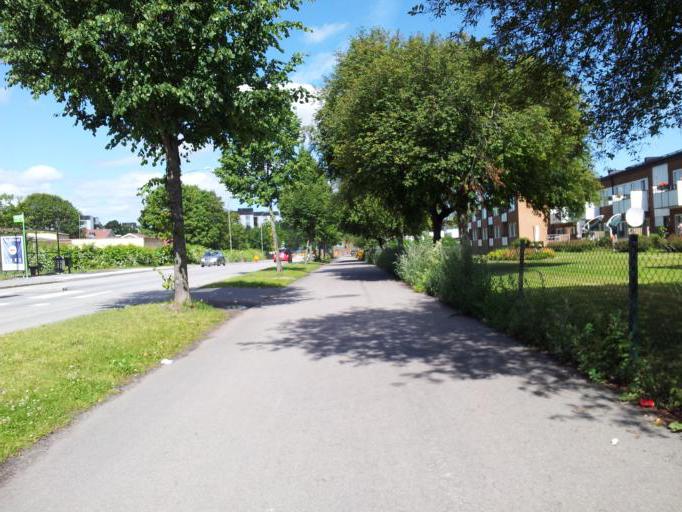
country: SE
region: Uppsala
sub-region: Uppsala Kommun
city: Uppsala
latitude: 59.8670
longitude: 17.6469
